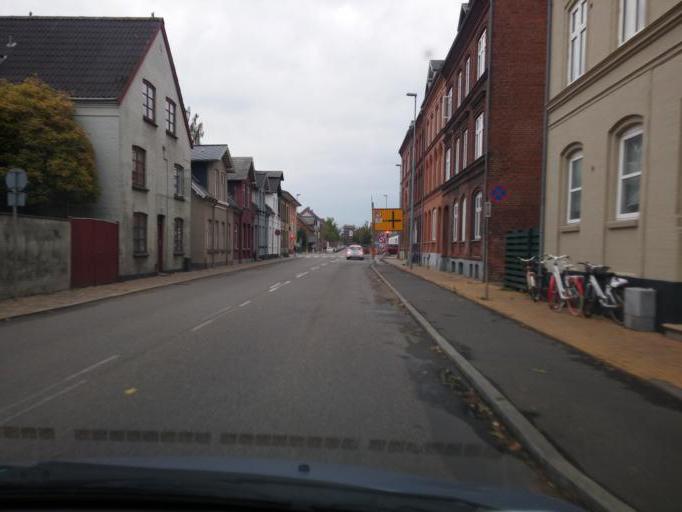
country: DK
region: South Denmark
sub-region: Odense Kommune
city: Odense
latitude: 55.3950
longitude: 10.3708
